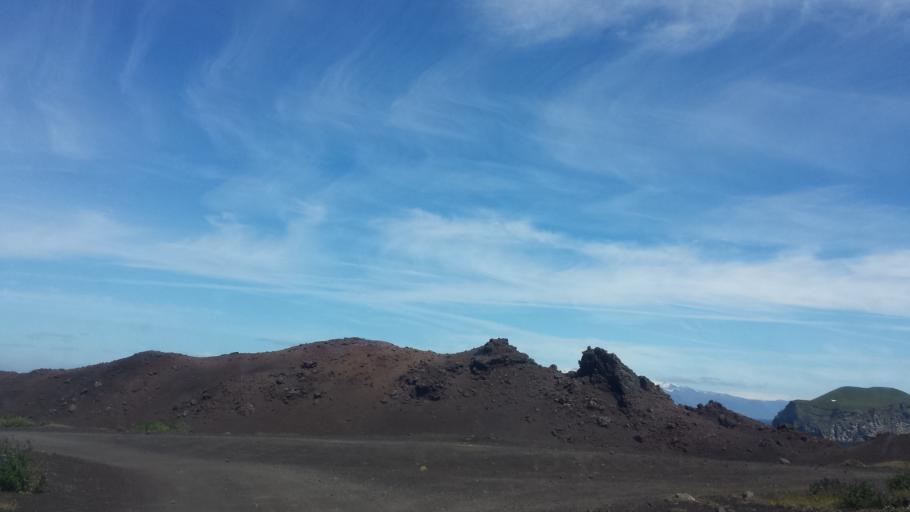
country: IS
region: South
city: Vestmannaeyjar
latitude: 63.4412
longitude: -20.2441
